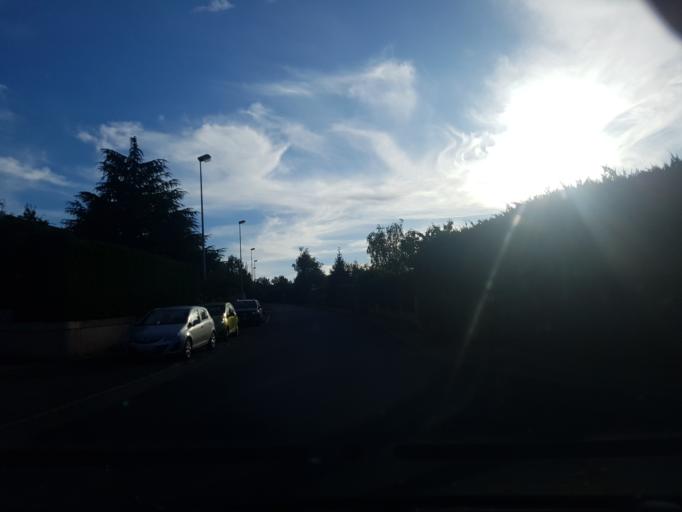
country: FR
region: Rhone-Alpes
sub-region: Departement du Rhone
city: Limas
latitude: 45.9730
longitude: 4.7068
